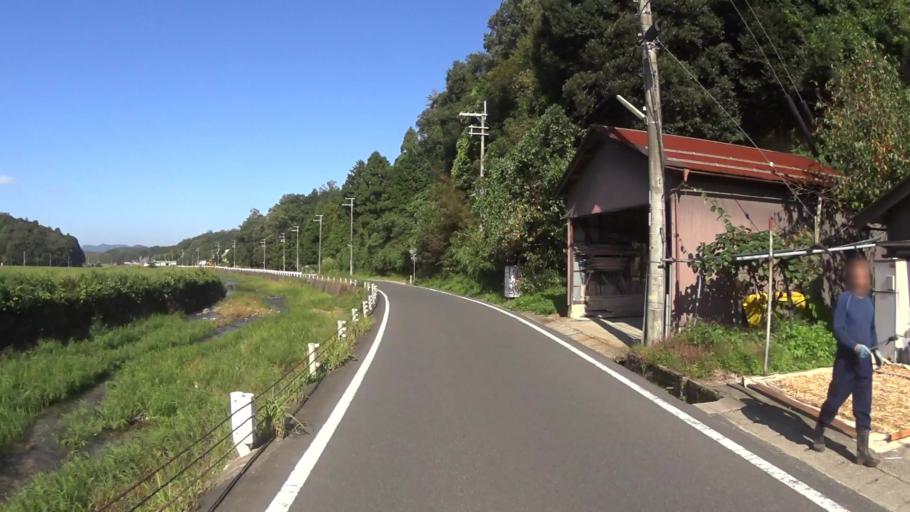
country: JP
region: Kyoto
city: Miyazu
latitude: 35.6588
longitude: 135.1105
